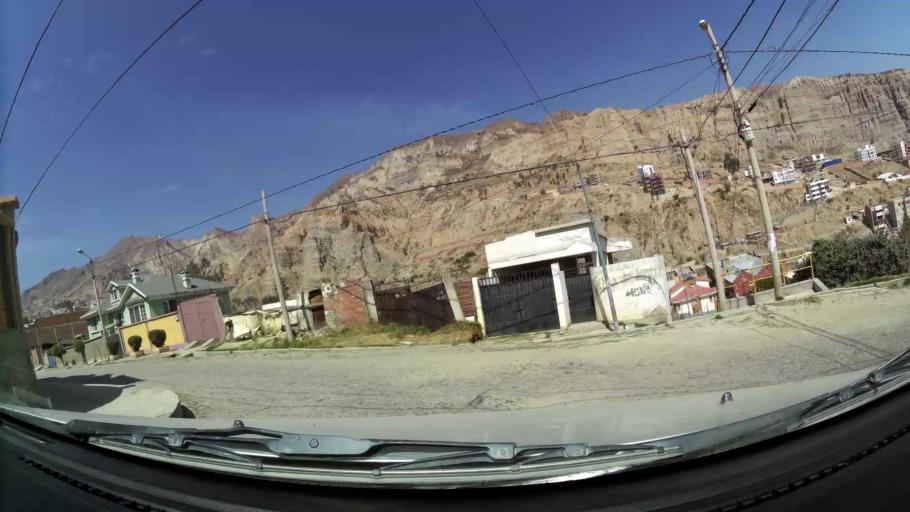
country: BO
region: La Paz
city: La Paz
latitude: -16.5454
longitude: -68.0614
